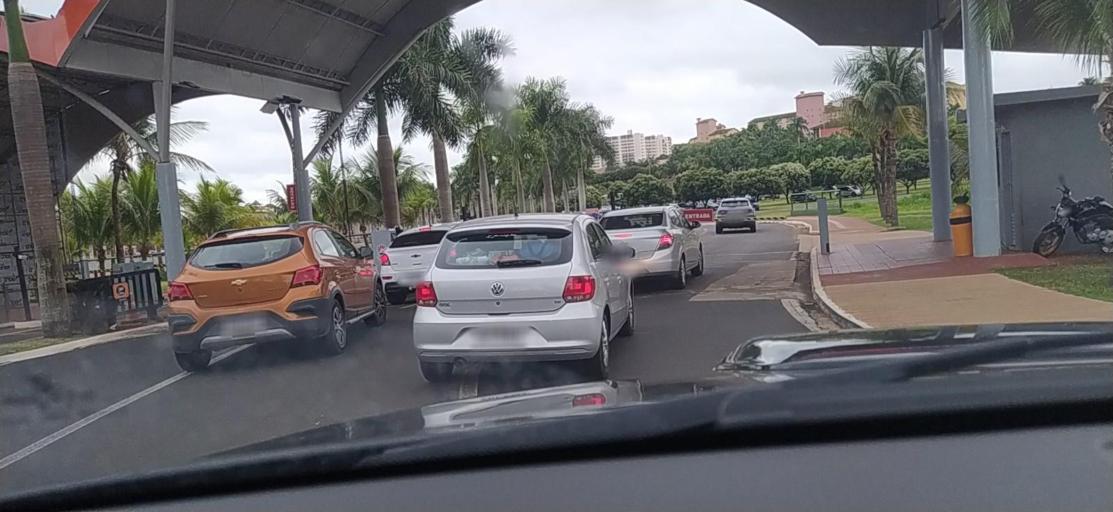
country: BR
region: Sao Paulo
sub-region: Olimpia
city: Olimpia
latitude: -20.7251
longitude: -48.9169
